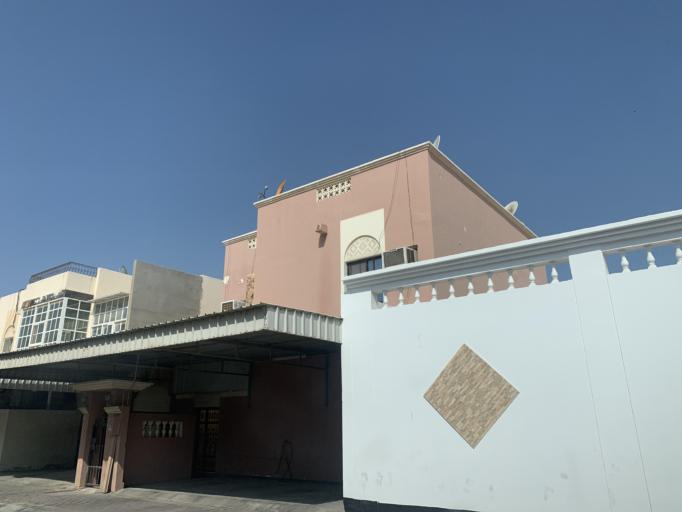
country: BH
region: Central Governorate
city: Madinat Hamad
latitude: 26.1316
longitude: 50.5026
